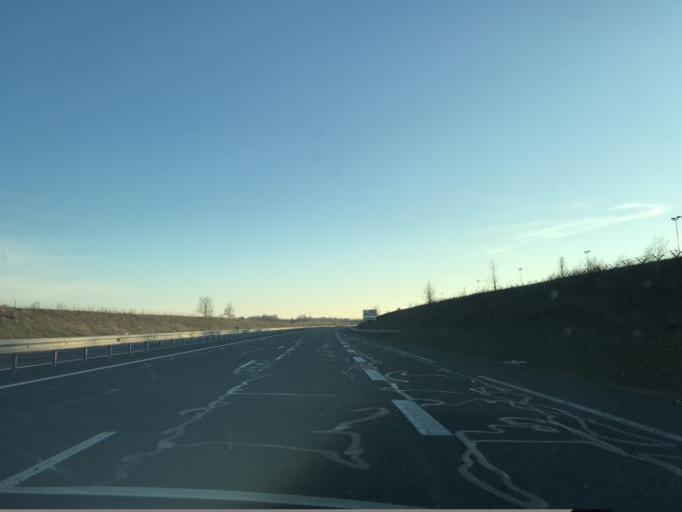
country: FR
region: Bourgogne
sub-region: Departement de l'Yonne
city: Egriselles-le-Bocage
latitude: 48.1610
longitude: 3.1750
